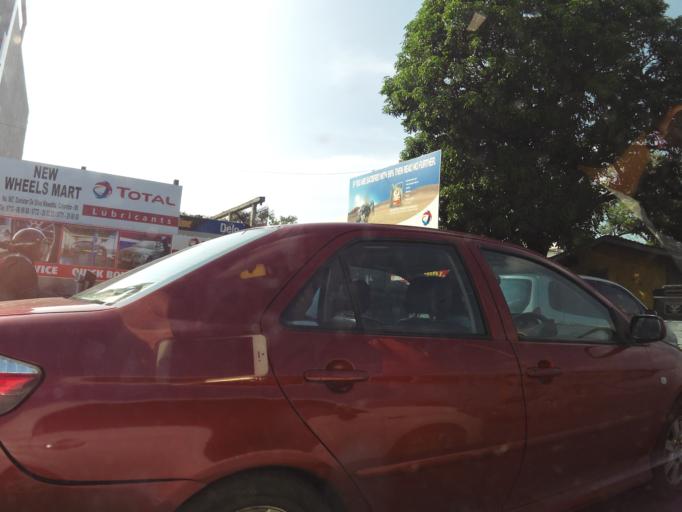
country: LK
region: Western
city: Kolonnawa
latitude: 6.9465
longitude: 79.8784
